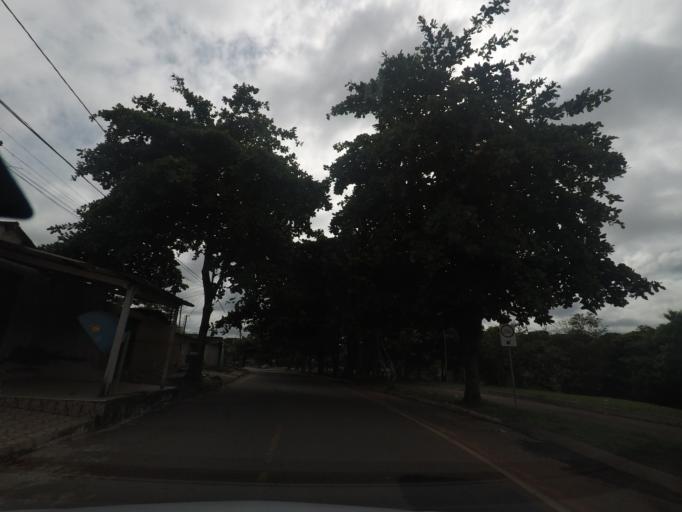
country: BR
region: Goias
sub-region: Goiania
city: Goiania
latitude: -16.7247
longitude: -49.2546
